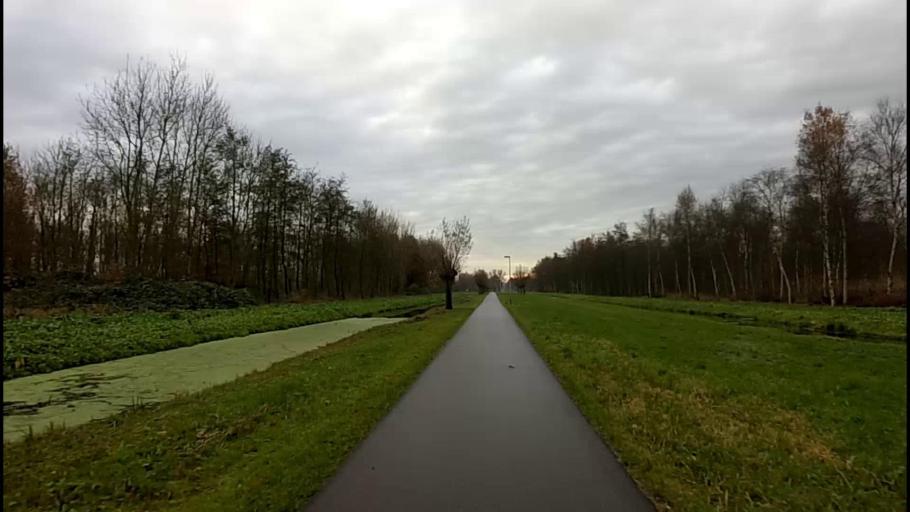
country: NL
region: South Holland
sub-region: Gemeente Krimpen aan den IJssel
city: Krimpen aan den IJssel
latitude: 51.9079
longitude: 4.6351
